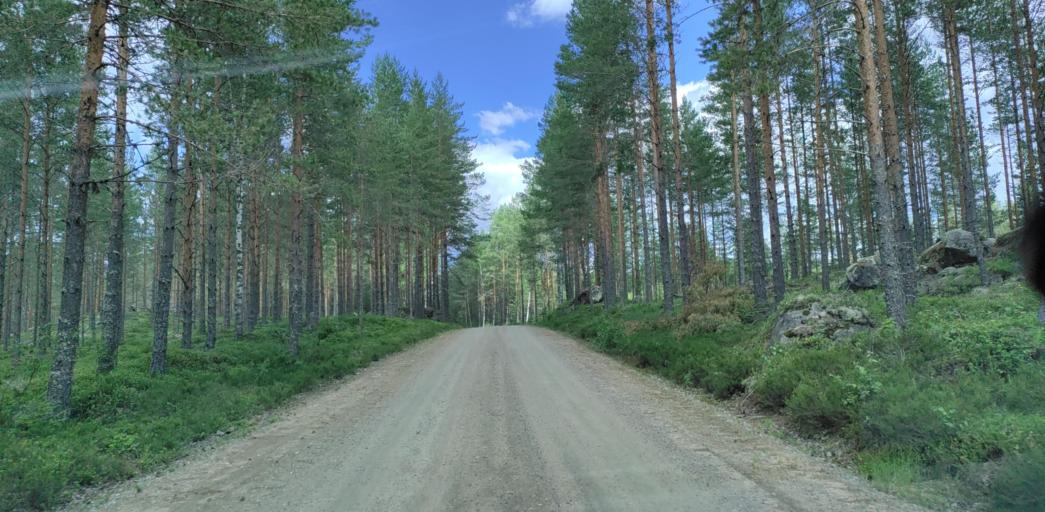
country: SE
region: Vaermland
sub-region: Hagfors Kommun
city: Ekshaerad
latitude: 60.0625
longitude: 13.2899
